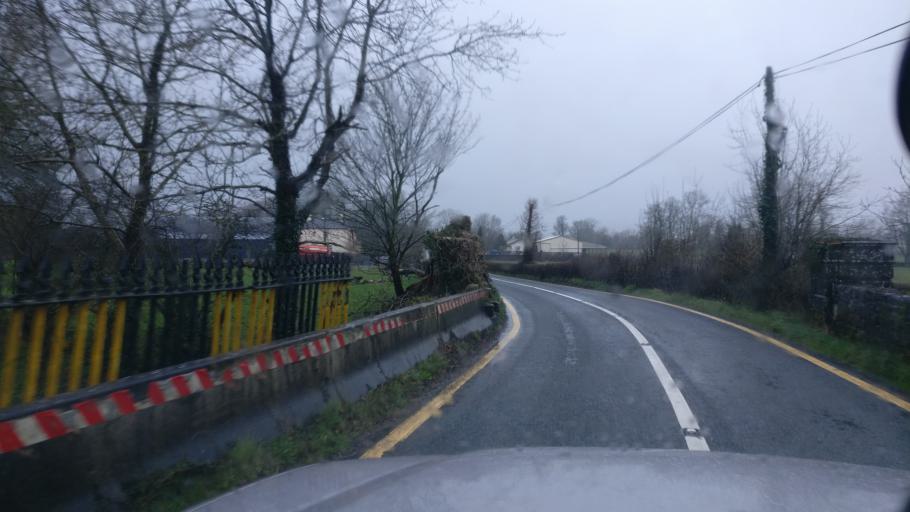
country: IE
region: Connaught
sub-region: County Galway
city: Loughrea
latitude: 53.1513
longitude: -8.4758
